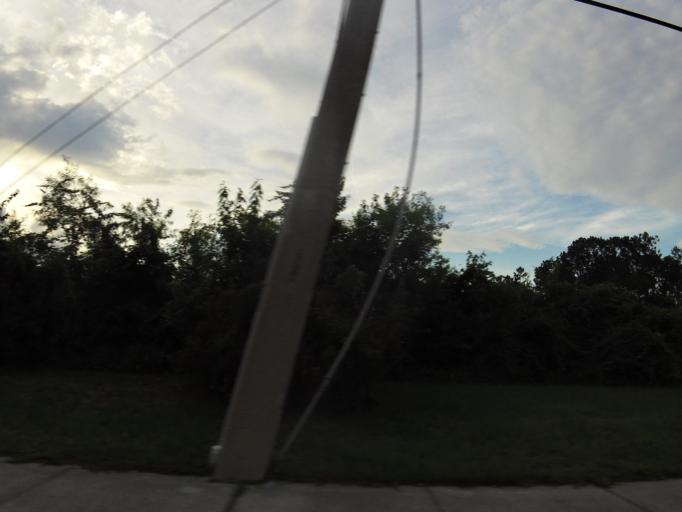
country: US
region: Florida
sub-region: Clay County
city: Bellair-Meadowbrook Terrace
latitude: 30.3023
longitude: -81.8153
